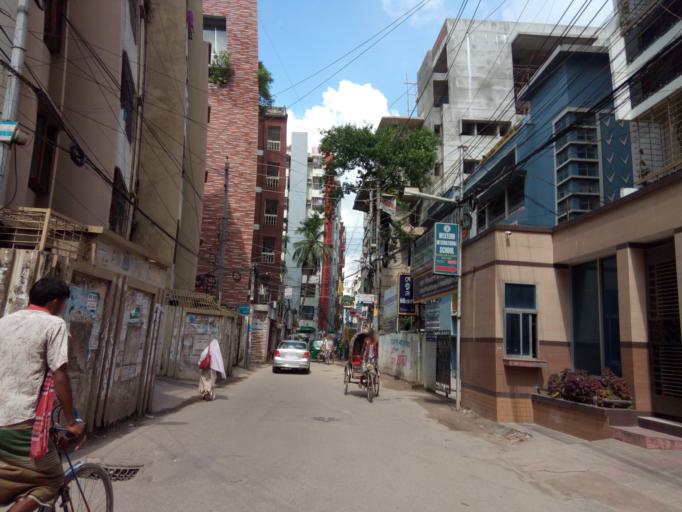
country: BD
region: Dhaka
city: Azimpur
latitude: 23.7416
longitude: 90.3861
